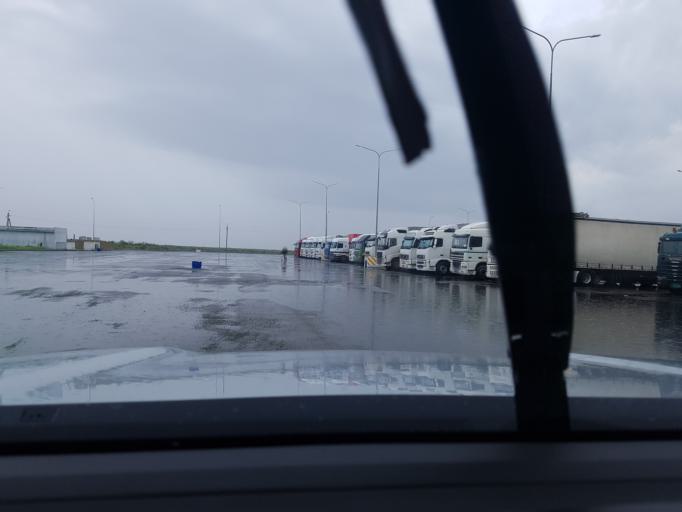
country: TM
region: Lebap
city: Farap
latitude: 39.2062
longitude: 63.6984
